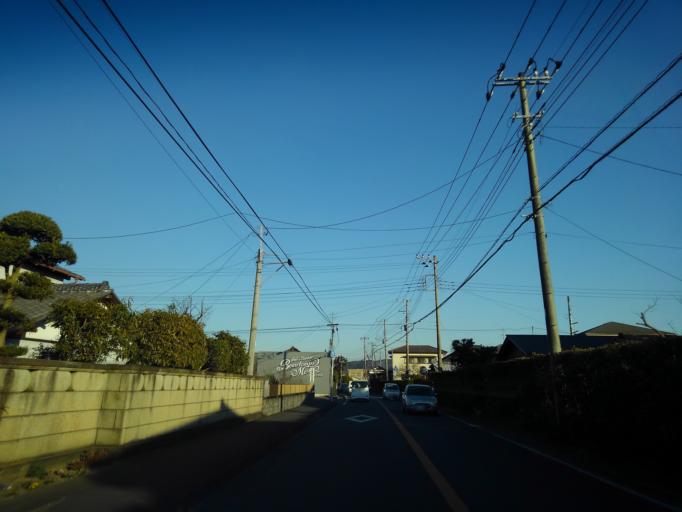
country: JP
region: Chiba
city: Kimitsu
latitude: 35.3047
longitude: 139.9658
